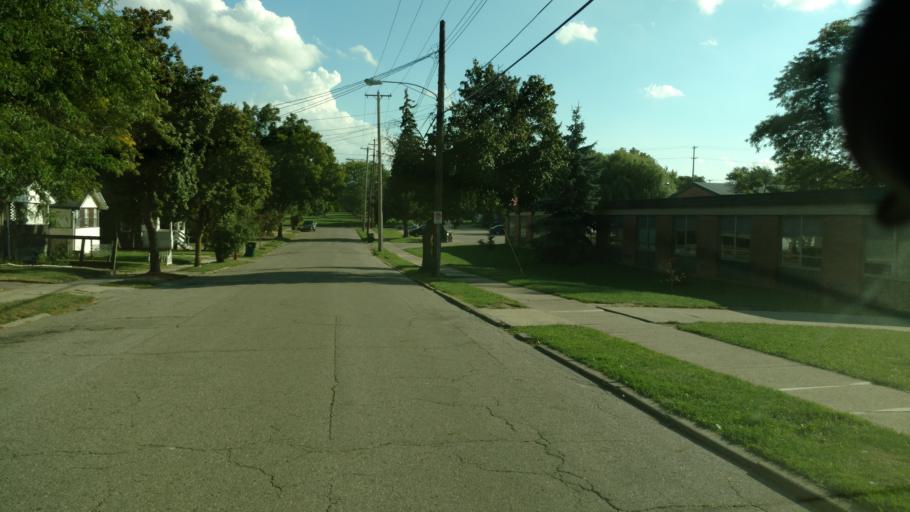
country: US
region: Michigan
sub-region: Ingham County
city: Lansing
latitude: 42.7495
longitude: -84.5657
